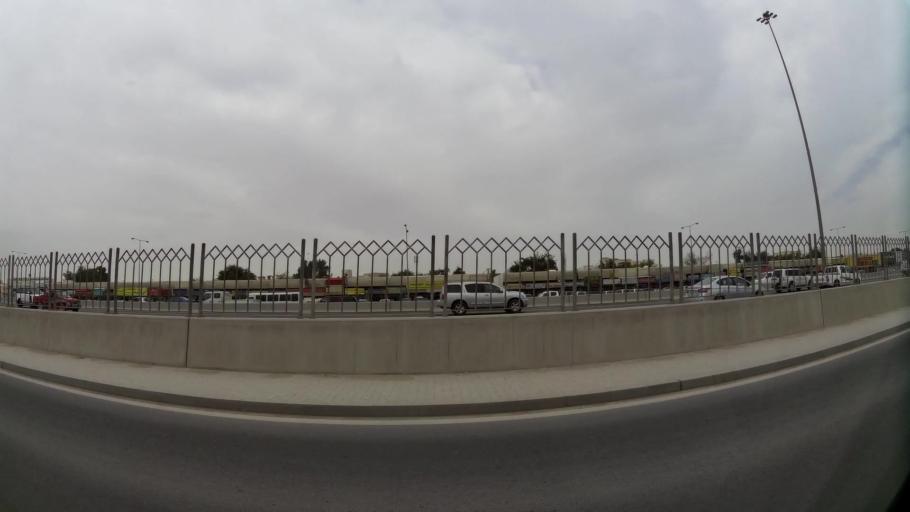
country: QA
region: Baladiyat ar Rayyan
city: Ar Rayyan
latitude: 25.2377
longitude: 51.4532
